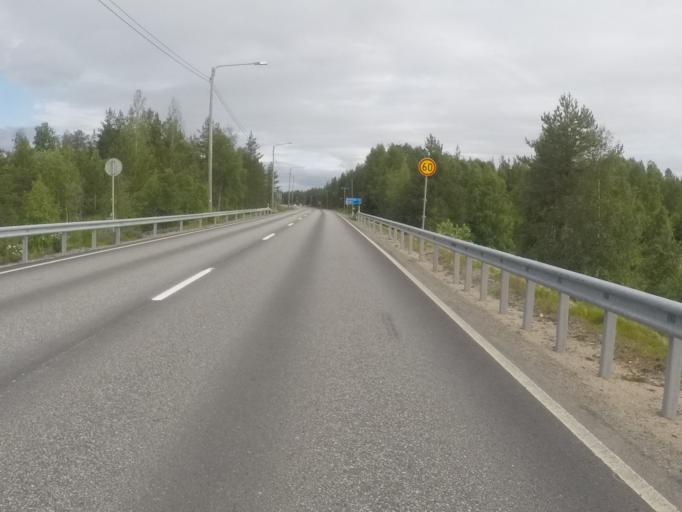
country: FI
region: Lapland
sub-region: Tunturi-Lappi
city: Kolari
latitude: 67.3515
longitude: 23.8277
